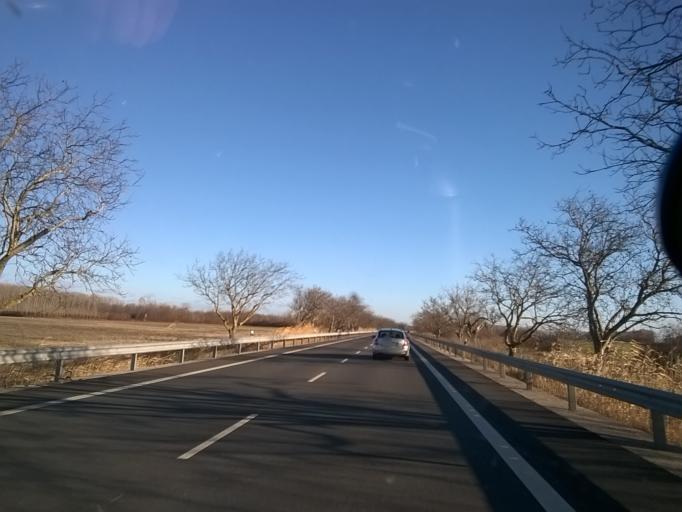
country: SK
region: Trnavsky
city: Sladkovicovo
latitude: 48.1969
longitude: 17.5795
